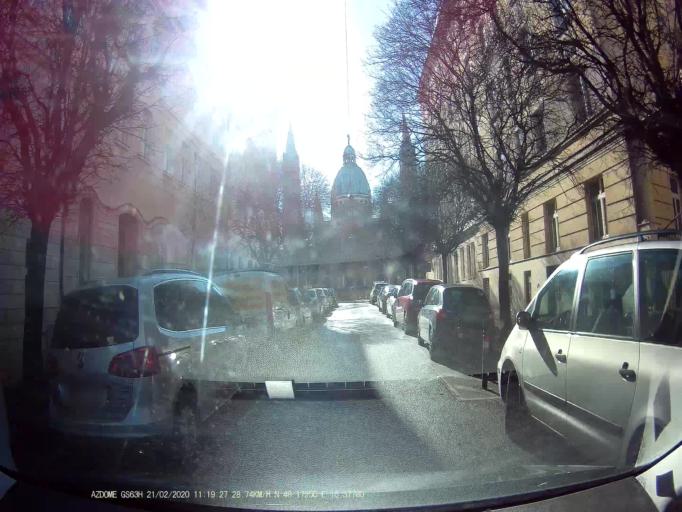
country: AT
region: Vienna
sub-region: Wien Stadt
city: Vienna
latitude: 48.1727
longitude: 16.3778
